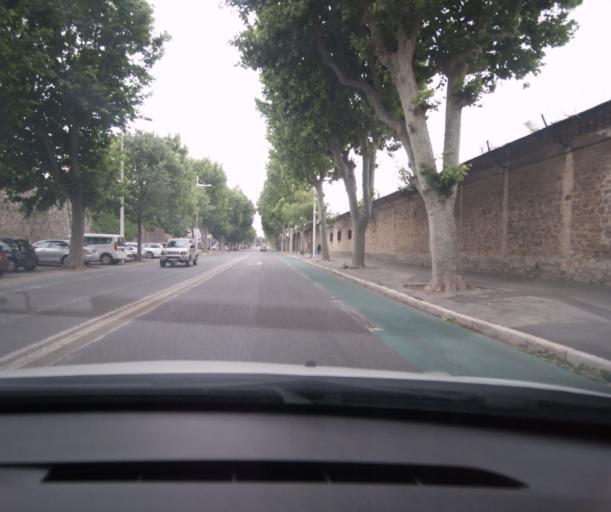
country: FR
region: Provence-Alpes-Cote d'Azur
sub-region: Departement du Var
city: Toulon
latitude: 43.1113
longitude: 5.9326
